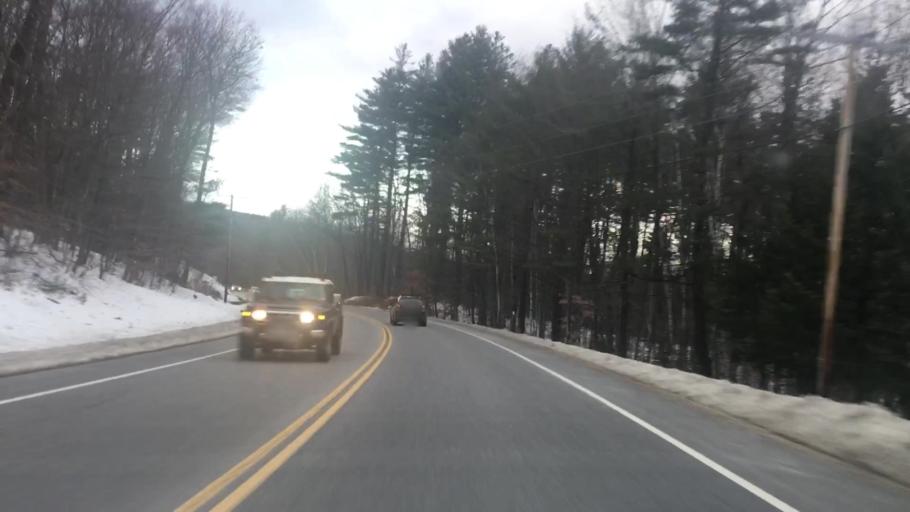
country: US
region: New Hampshire
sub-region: Hillsborough County
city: Antrim
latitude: 43.0851
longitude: -71.9649
